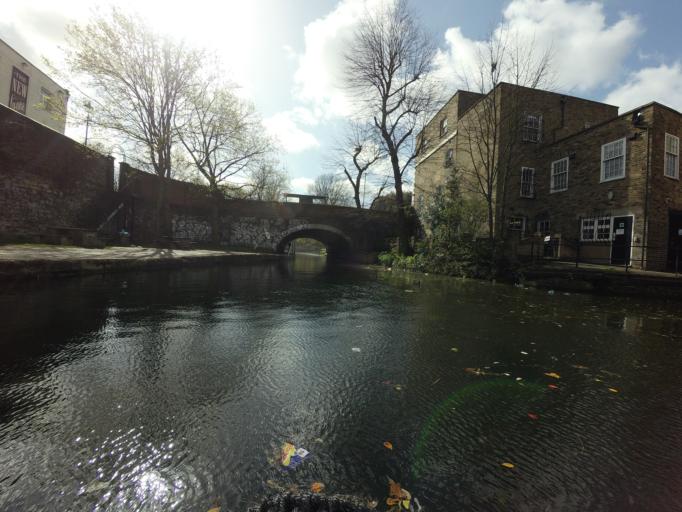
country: GB
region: England
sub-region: Greater London
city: Bethnal Green
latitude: 51.5246
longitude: -0.0373
